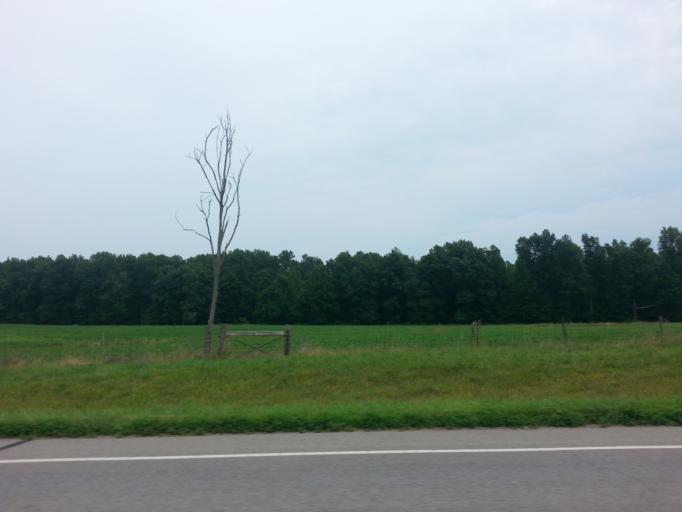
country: US
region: Ohio
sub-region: Brown County
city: Georgetown
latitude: 38.8842
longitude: -83.8916
